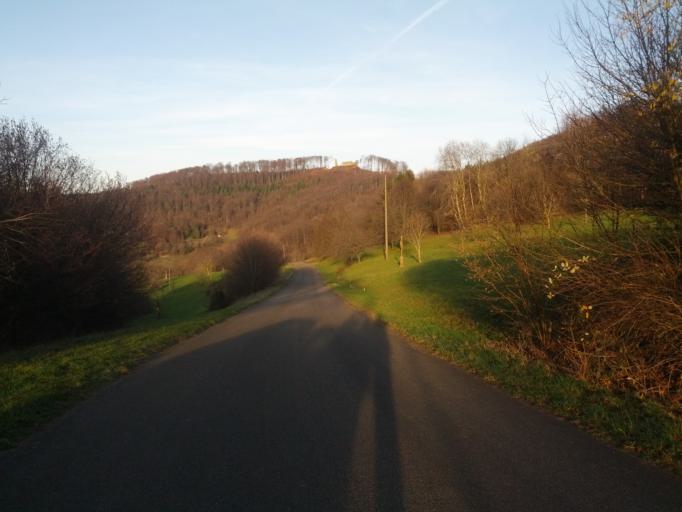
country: DE
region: Baden-Wuerttemberg
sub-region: Freiburg Region
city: Ebringen
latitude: 47.9519
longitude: 7.7879
